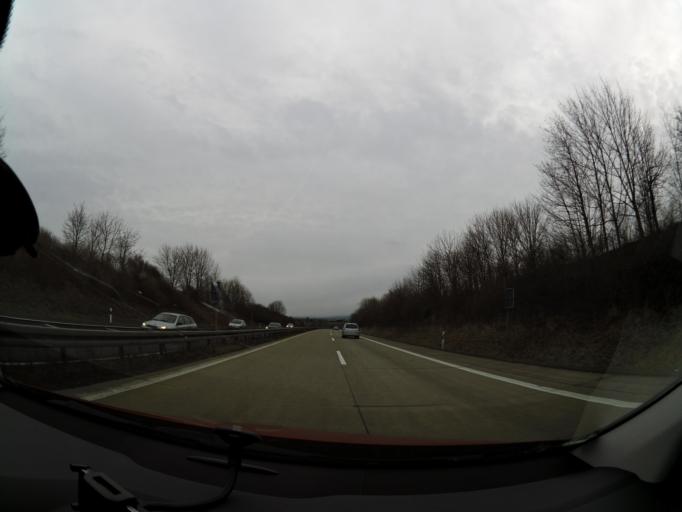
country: DE
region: Lower Saxony
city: Schladen
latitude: 51.9987
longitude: 10.5502
